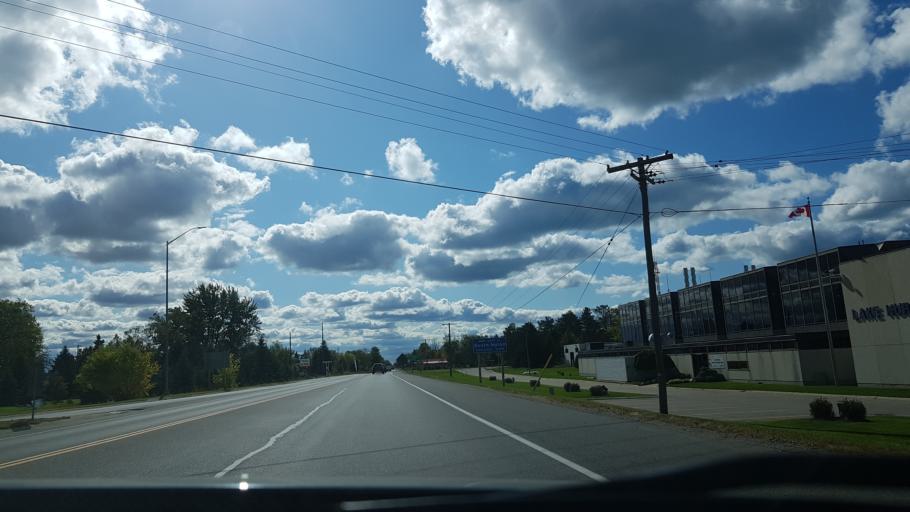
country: CA
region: Ontario
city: Bluewater
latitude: 43.3354
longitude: -81.7379
